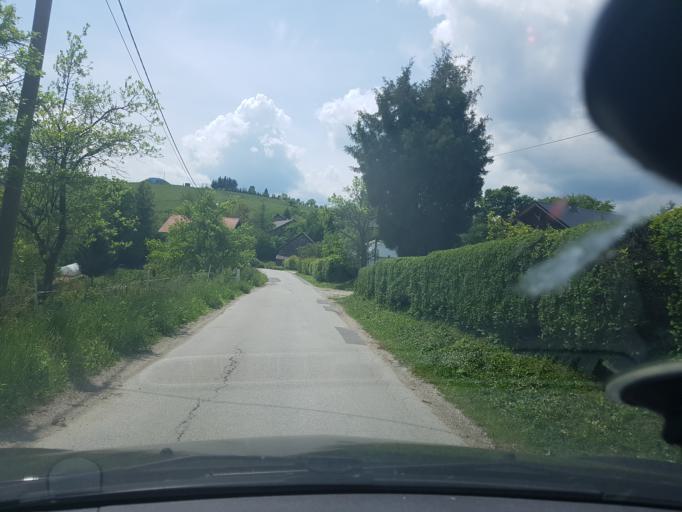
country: SI
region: Rogatec
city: Rogatec
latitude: 46.2139
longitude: 15.6998
